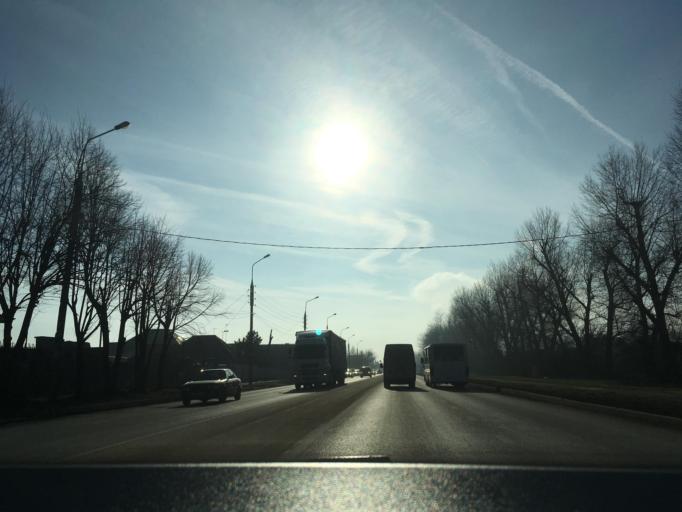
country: RU
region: Krasnodarskiy
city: Krasnodar
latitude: 45.1029
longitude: 39.0129
